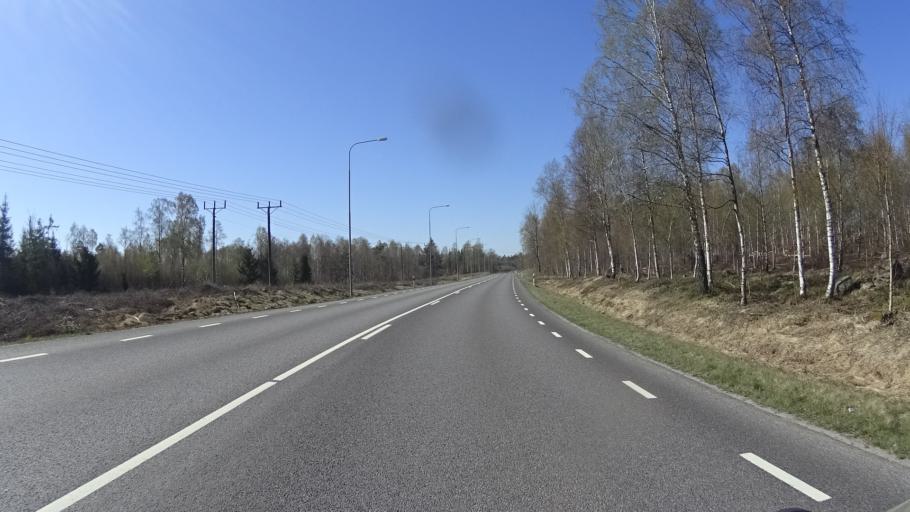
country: SE
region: Kronoberg
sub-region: Ljungby Kommun
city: Ljungby
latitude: 56.8308
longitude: 13.9742
